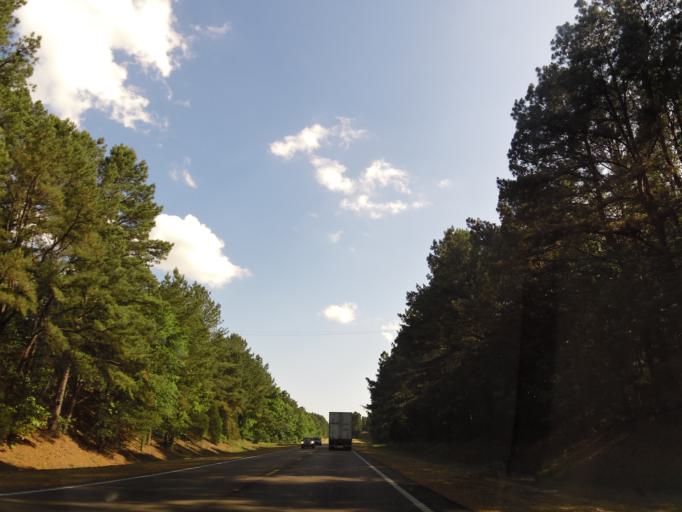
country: US
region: Mississippi
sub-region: Lafayette County
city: Oxford
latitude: 34.3255
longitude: -89.5175
